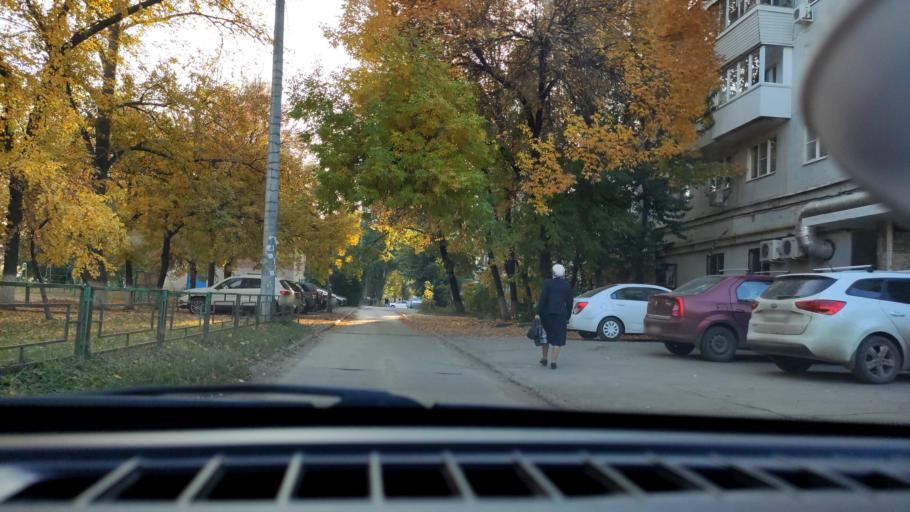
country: RU
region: Samara
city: Samara
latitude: 53.2265
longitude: 50.2034
